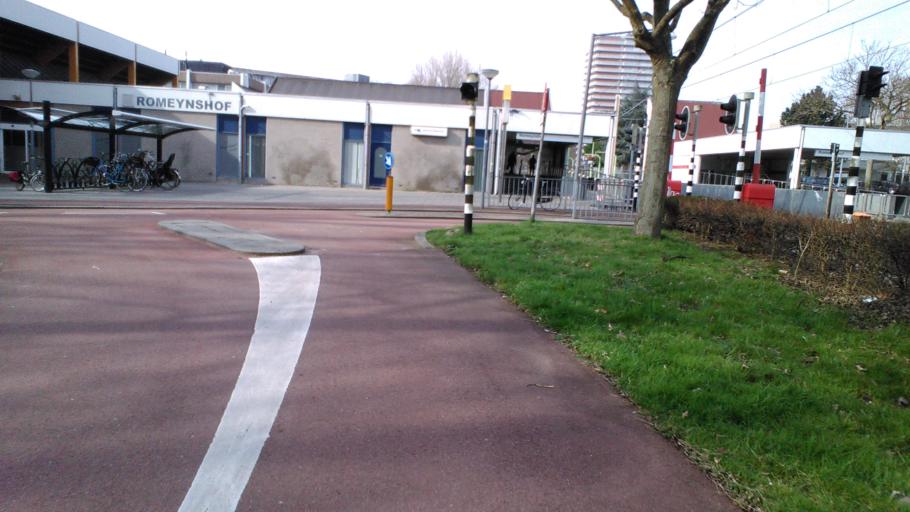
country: NL
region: South Holland
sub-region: Gemeente Rotterdam
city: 's-Gravenland
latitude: 51.9616
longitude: 4.5440
